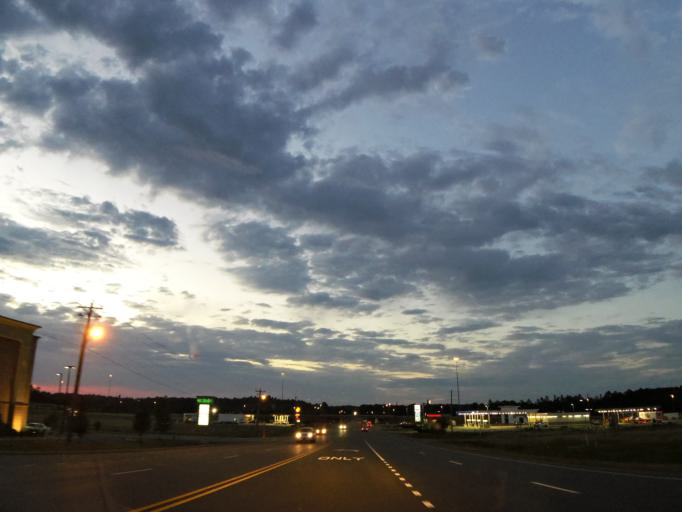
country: US
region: Alabama
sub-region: Marion County
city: Winfield
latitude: 33.9855
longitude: -87.7762
